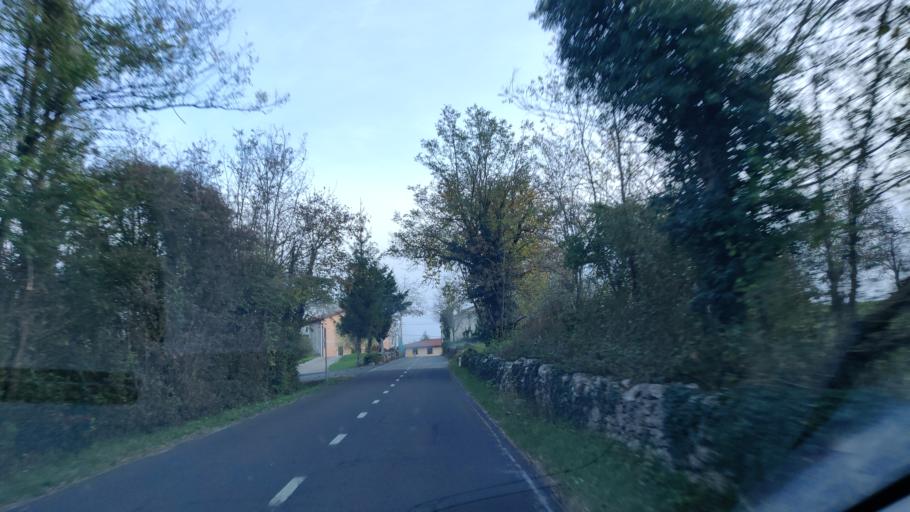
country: SI
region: Sezana
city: Sezana
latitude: 45.7678
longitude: 13.8808
